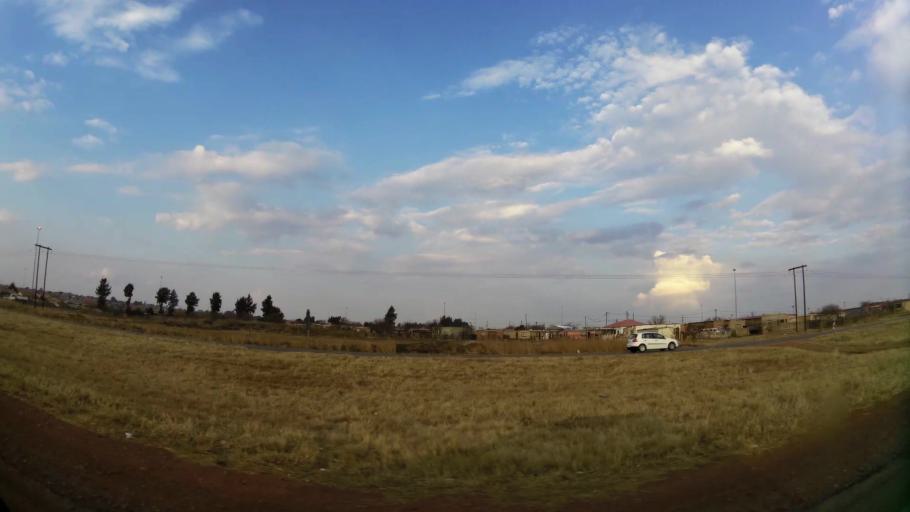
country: ZA
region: Gauteng
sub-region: City of Johannesburg Metropolitan Municipality
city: Orange Farm
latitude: -26.5921
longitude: 27.8209
